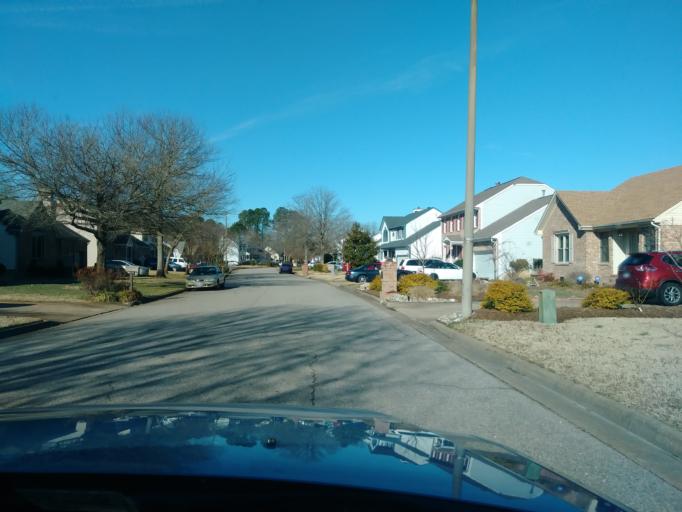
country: US
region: Virginia
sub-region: City of Chesapeake
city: Chesapeake
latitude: 36.7533
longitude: -76.2107
